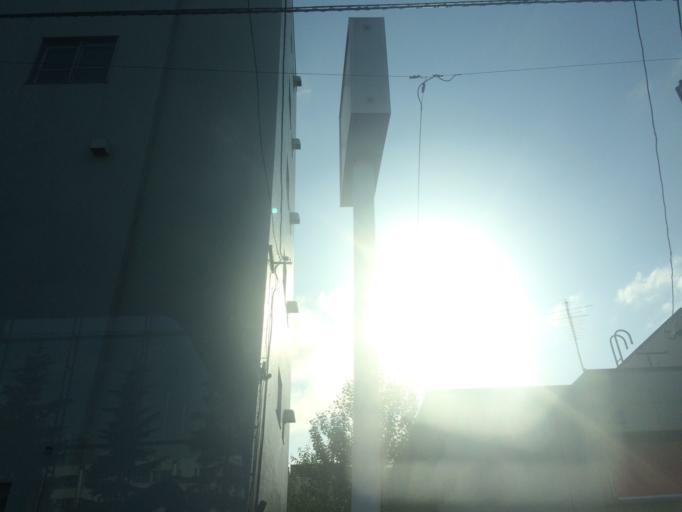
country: JP
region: Hokkaido
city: Sapporo
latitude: 43.0368
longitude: 141.3512
